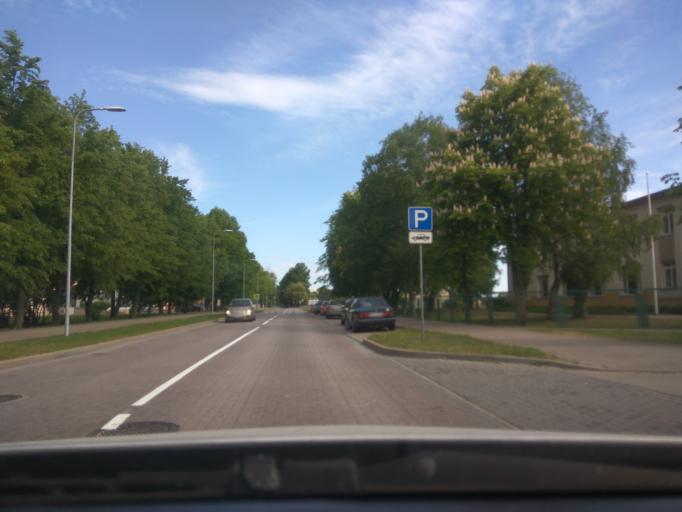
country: LV
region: Ventspils
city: Ventspils
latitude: 57.3931
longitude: 21.5734
